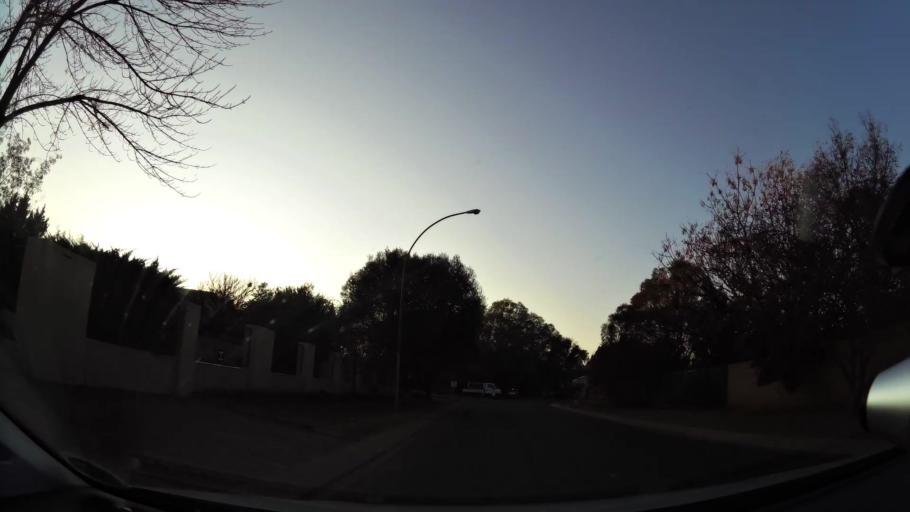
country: ZA
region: Orange Free State
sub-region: Mangaung Metropolitan Municipality
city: Bloemfontein
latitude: -29.1032
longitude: 26.1557
